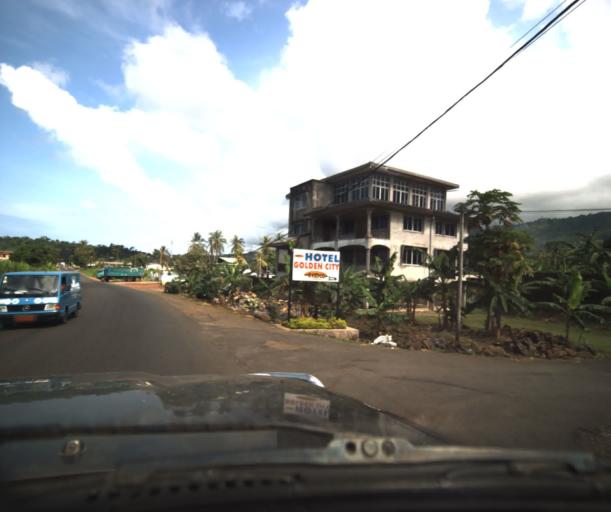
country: CM
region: South-West Province
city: Limbe
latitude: 4.0156
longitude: 9.1489
